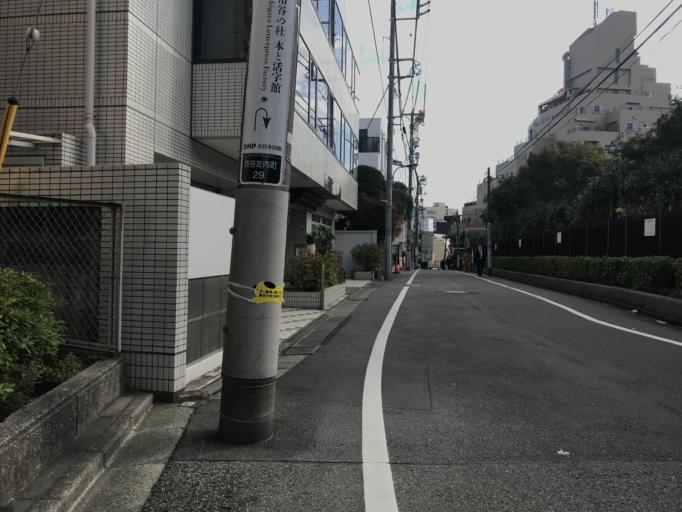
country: JP
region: Tokyo
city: Tokyo
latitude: 35.6940
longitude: 139.7334
